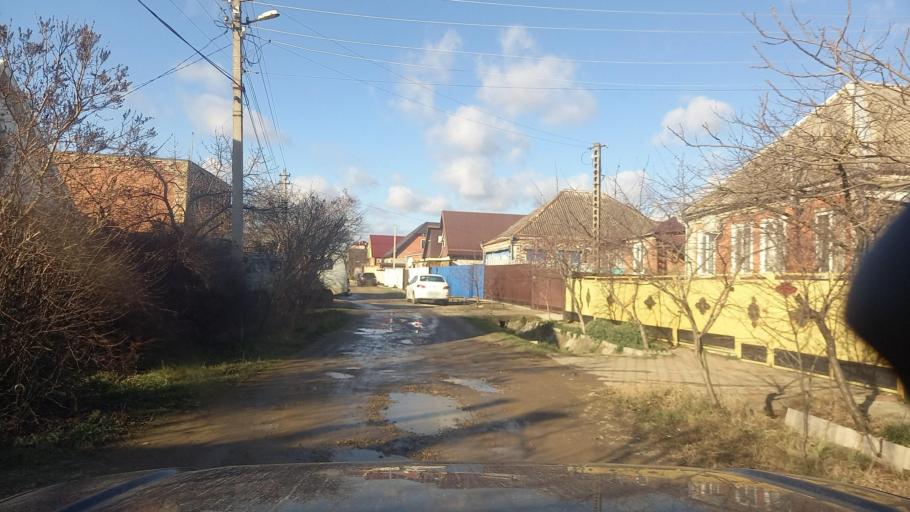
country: RU
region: Adygeya
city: Yablonovskiy
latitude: 44.9928
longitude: 38.9458
